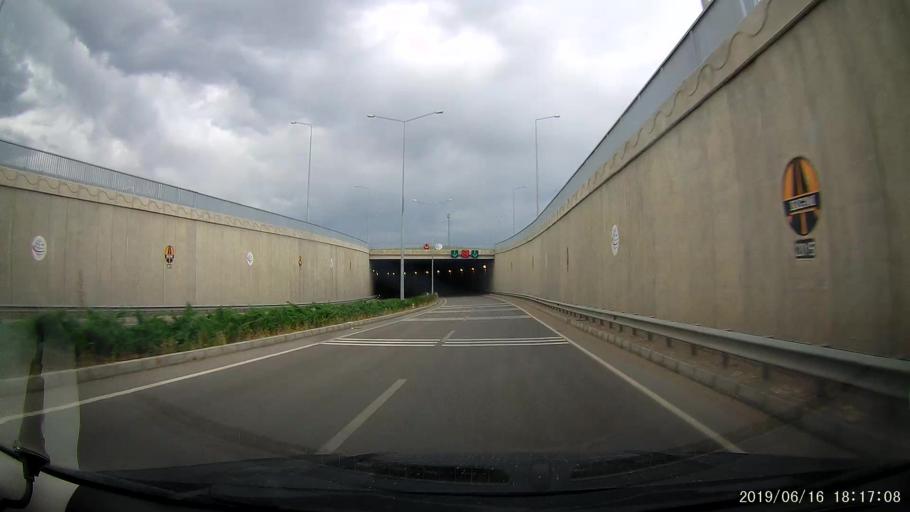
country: TR
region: Erzincan
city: Erzincan
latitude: 39.7326
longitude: 39.5374
